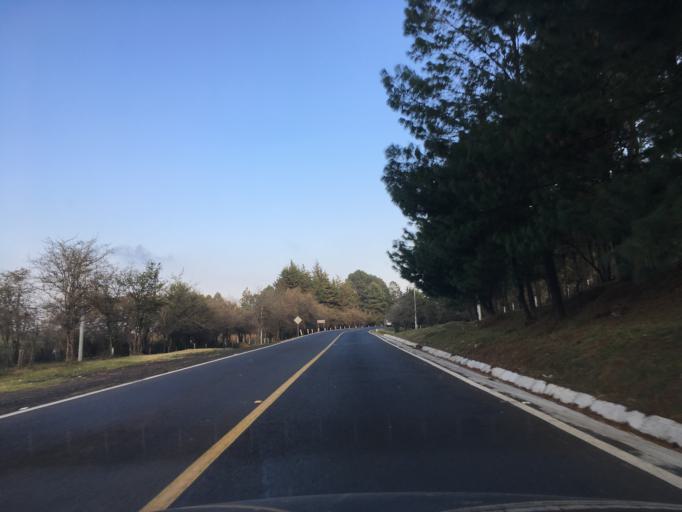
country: MX
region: Michoacan
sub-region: Patzcuaro
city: Santa Maria Huiramangaro (San Juan Tumbio)
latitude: 19.5005
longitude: -101.7610
